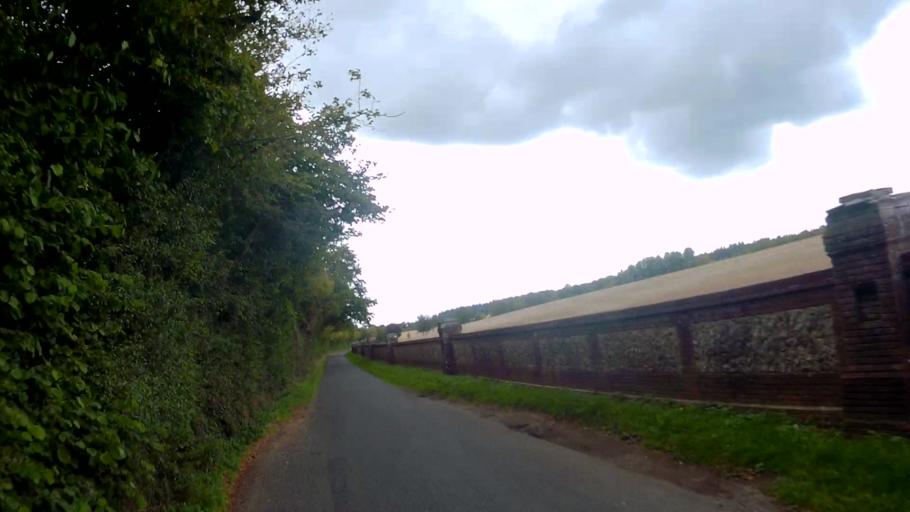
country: GB
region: England
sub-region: Hampshire
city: Overton
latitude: 51.1965
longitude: -1.2818
